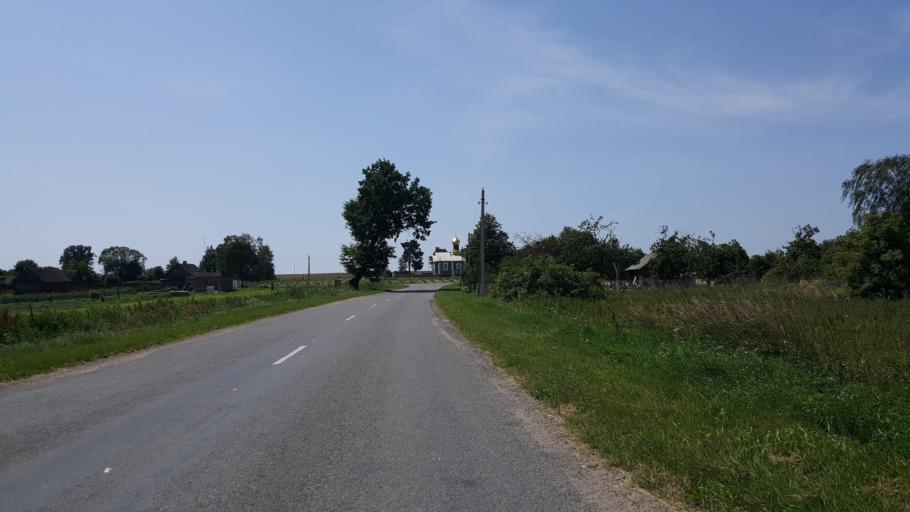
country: BY
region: Brest
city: Vysokaye
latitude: 52.3579
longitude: 23.5107
